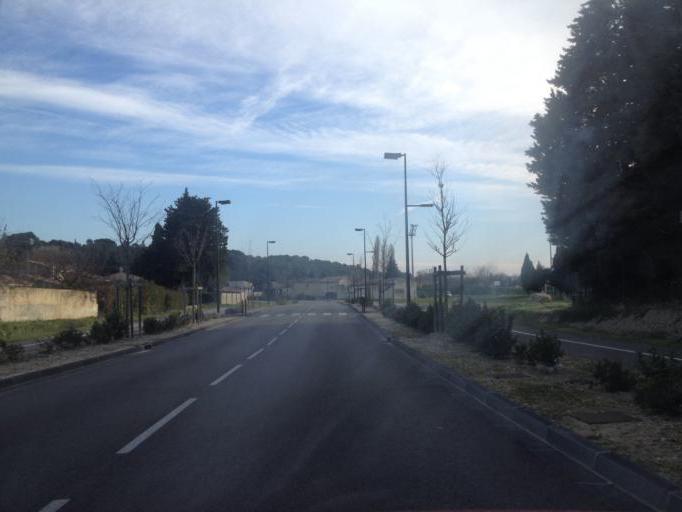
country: FR
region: Provence-Alpes-Cote d'Azur
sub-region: Departement du Vaucluse
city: Orange
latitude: 44.1278
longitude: 4.7986
